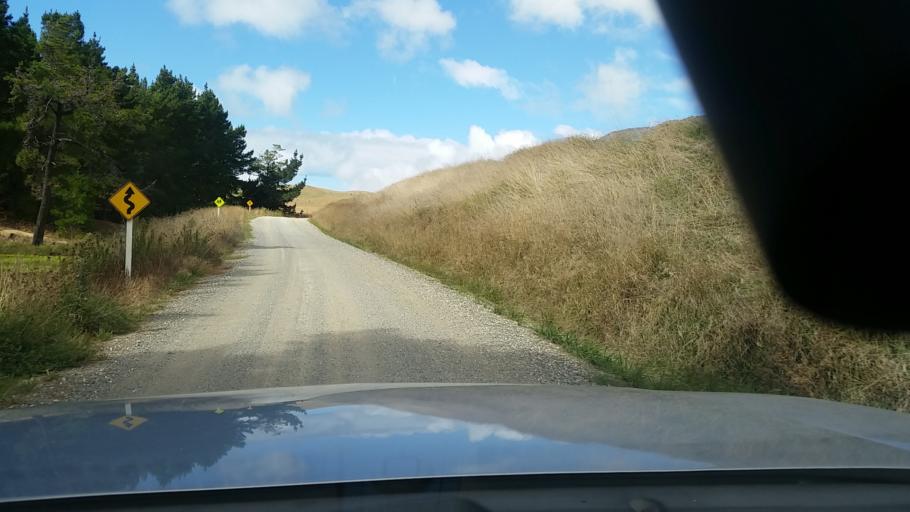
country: NZ
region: Marlborough
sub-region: Marlborough District
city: Blenheim
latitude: -41.6915
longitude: 174.1422
